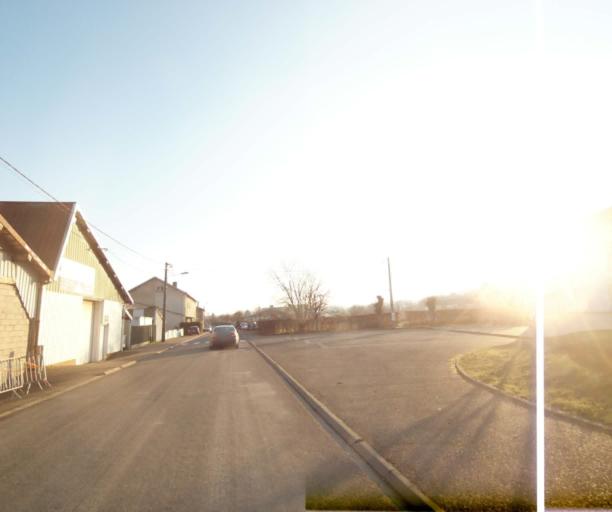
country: FR
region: Champagne-Ardenne
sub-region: Departement de la Haute-Marne
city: Bienville
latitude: 48.5831
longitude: 5.0453
